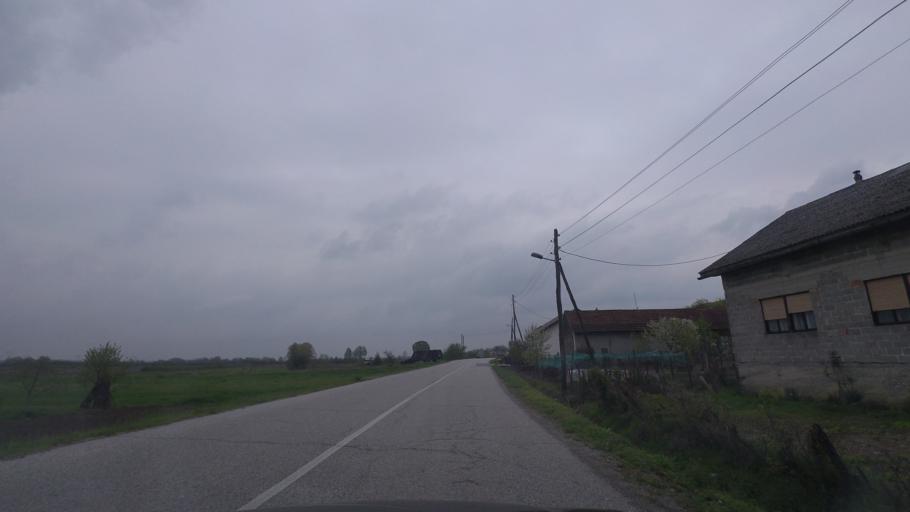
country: HR
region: Zagrebacka
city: Jastrebarsko
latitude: 45.6186
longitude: 15.5762
